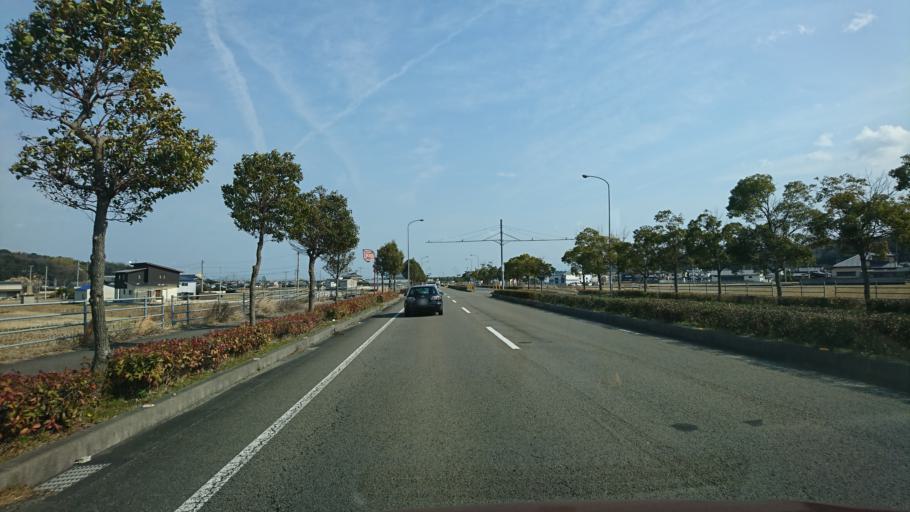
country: JP
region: Ehime
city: Saijo
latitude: 34.0194
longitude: 133.0214
